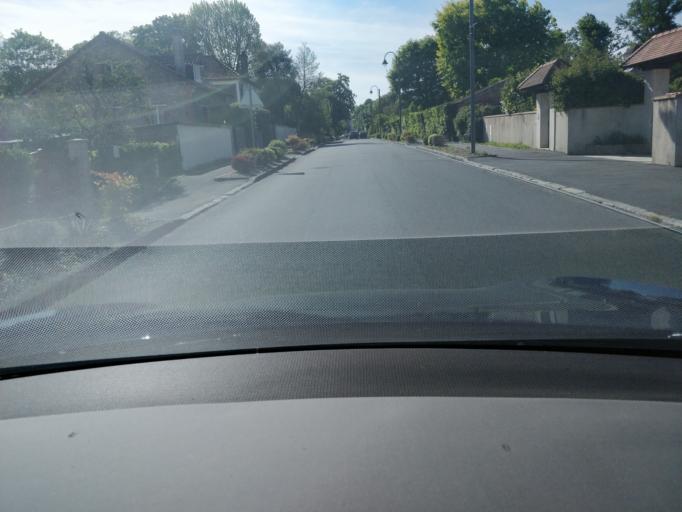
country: FR
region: Ile-de-France
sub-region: Departement de l'Essonne
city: Forges-les-Bains
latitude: 48.6264
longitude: 2.1086
